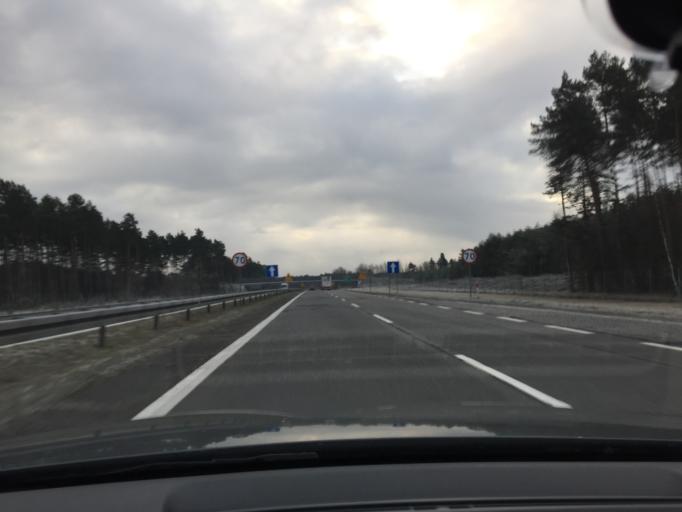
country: PL
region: Lubusz
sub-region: Powiat zarski
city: Trzebiel
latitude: 51.6334
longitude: 14.8749
